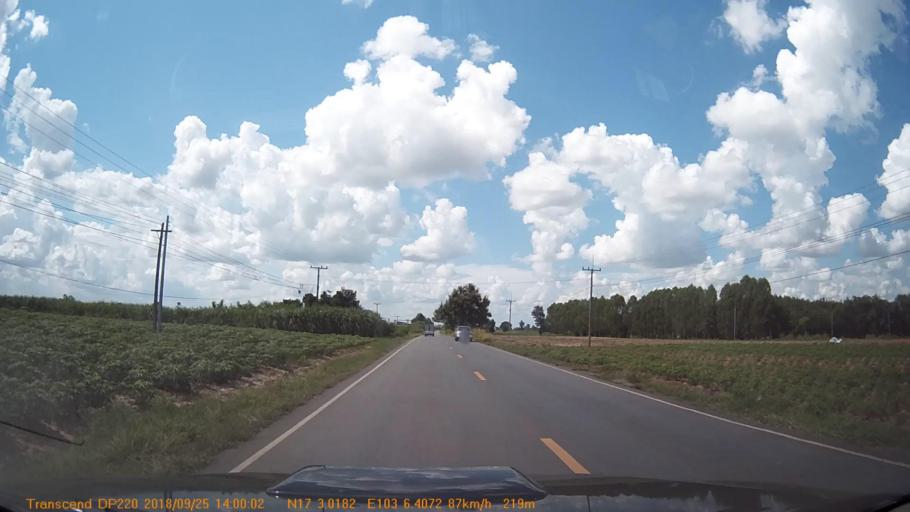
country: TH
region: Changwat Udon Thani
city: Kumphawapi
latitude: 17.0506
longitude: 103.1069
